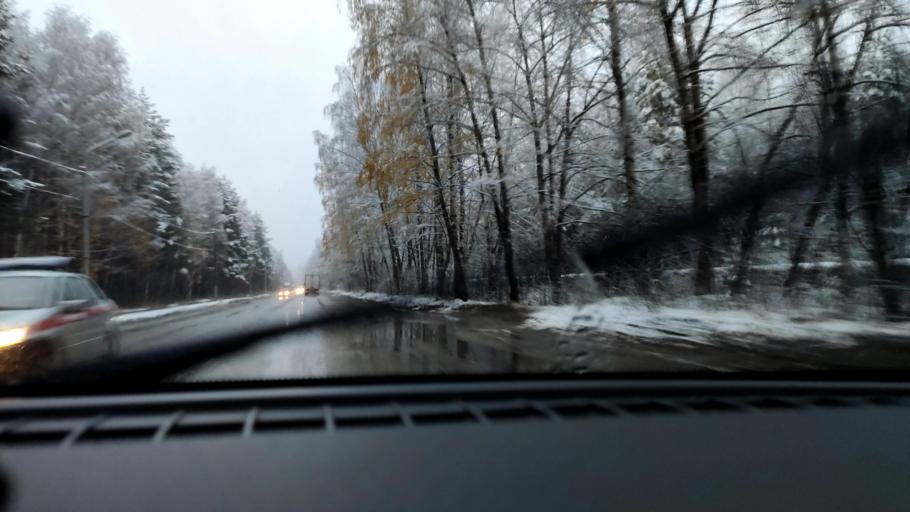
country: RU
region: Perm
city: Overyata
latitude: 58.0140
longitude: 55.9109
